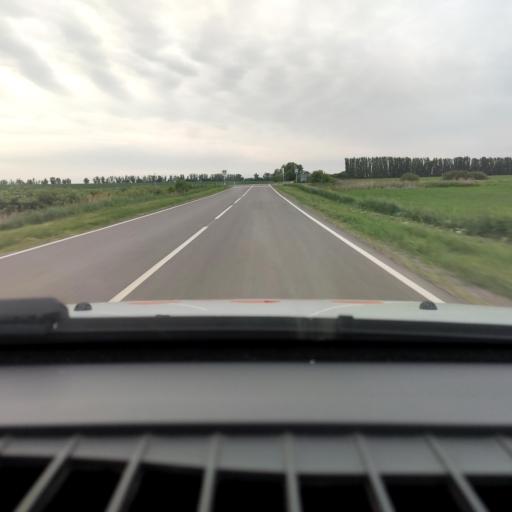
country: RU
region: Voronezj
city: Podkletnoye
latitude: 51.5859
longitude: 39.5082
